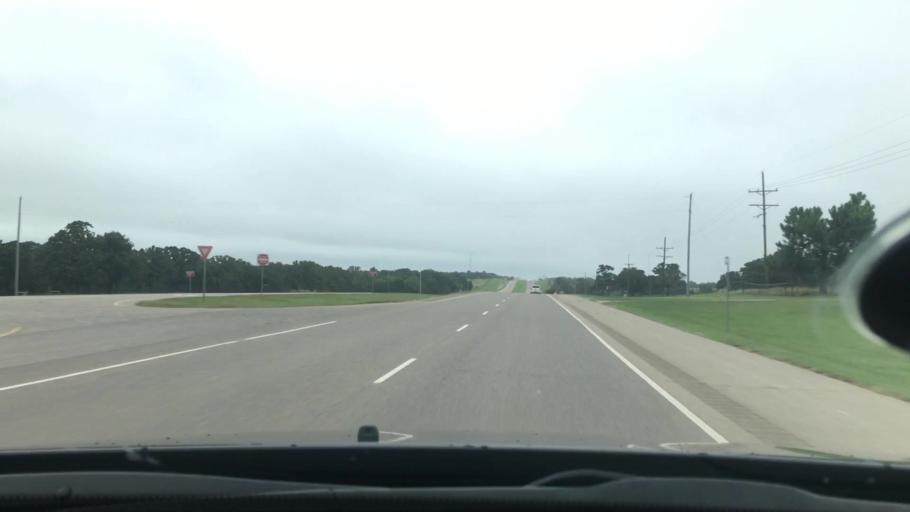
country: US
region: Oklahoma
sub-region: Seminole County
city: Seminole
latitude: 35.3545
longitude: -96.6715
